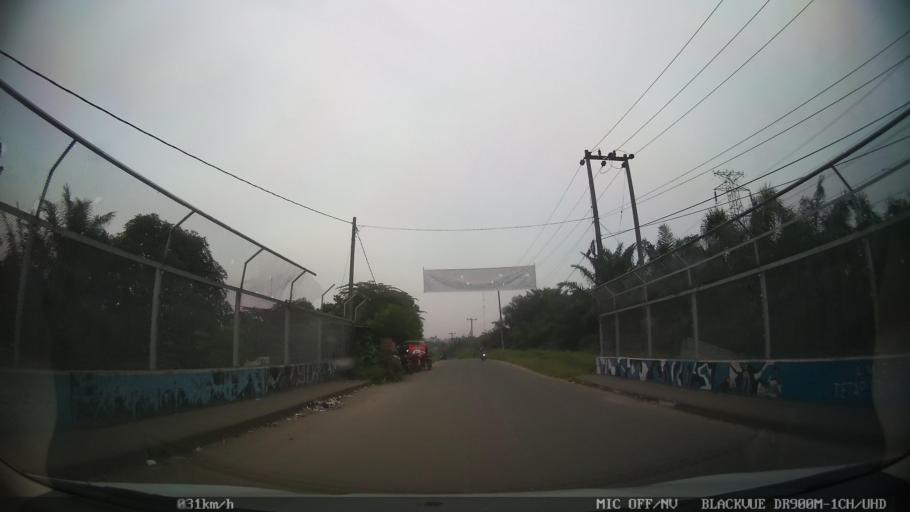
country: ID
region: North Sumatra
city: Deli Tua
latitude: 3.5517
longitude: 98.7255
